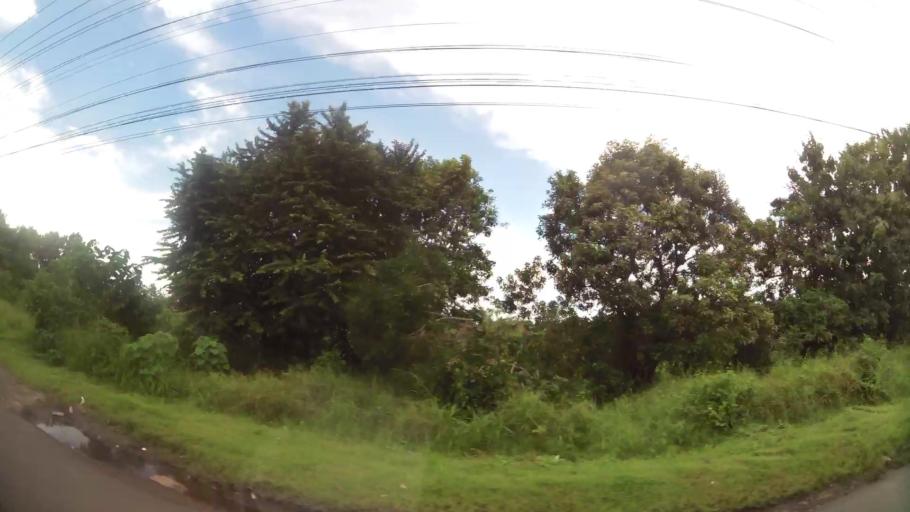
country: PA
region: Panama
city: Tocumen
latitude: 9.0695
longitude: -79.3988
